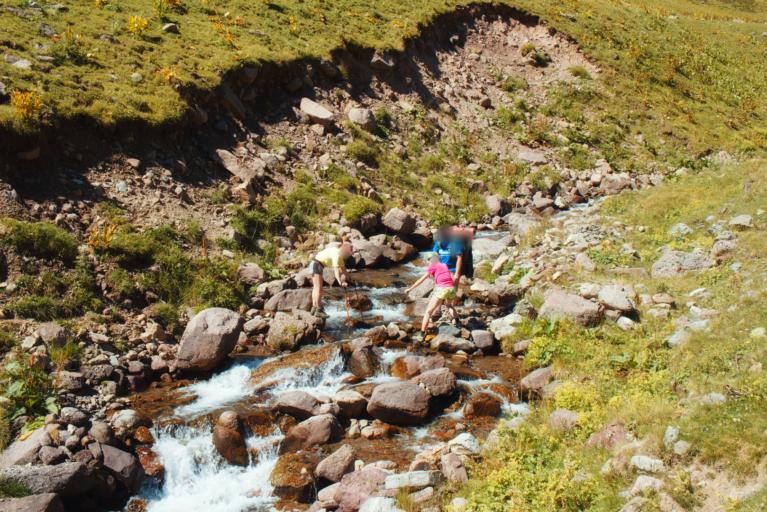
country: RU
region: Karachayevo-Cherkesiya
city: Mednogorskiy
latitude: 43.6055
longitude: 41.0870
